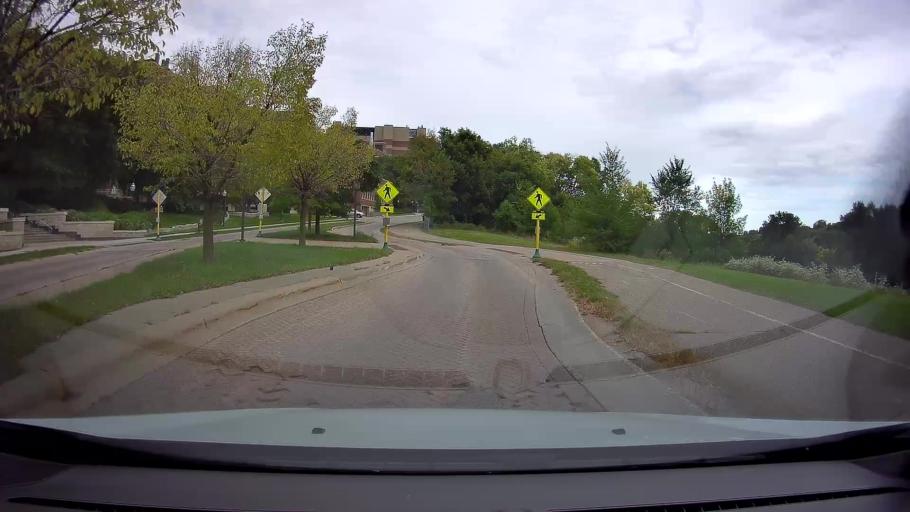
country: US
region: Minnesota
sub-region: Hennepin County
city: Minneapolis
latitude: 44.9712
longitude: -93.2355
